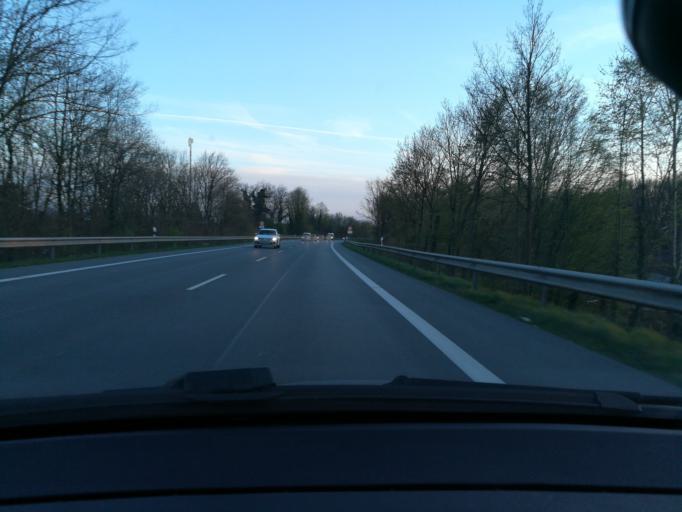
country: DE
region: North Rhine-Westphalia
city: Halle
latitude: 52.0619
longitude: 8.3476
